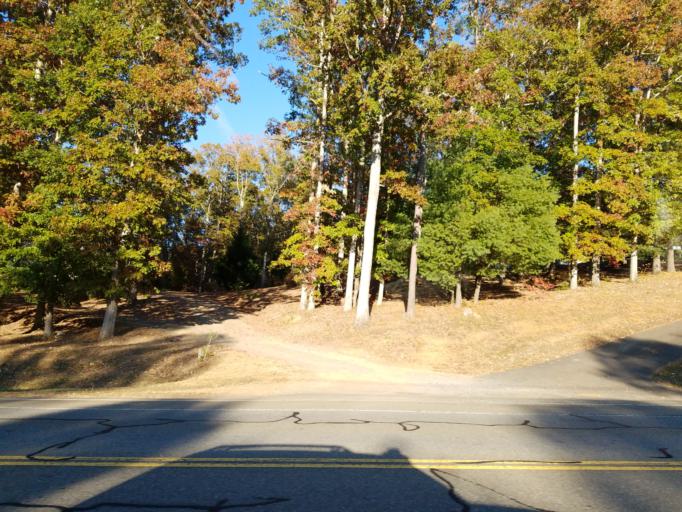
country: US
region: Georgia
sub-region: Gilmer County
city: Ellijay
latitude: 34.6658
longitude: -84.4515
